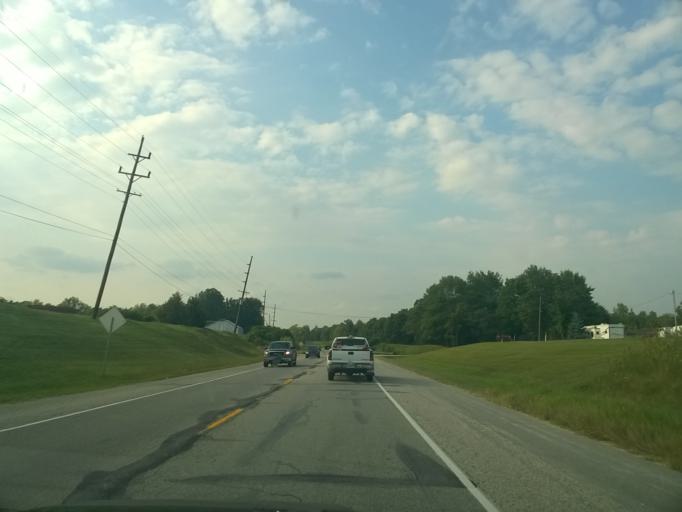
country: US
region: Indiana
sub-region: Putnam County
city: Cloverdale
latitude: 39.5465
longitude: -86.8071
